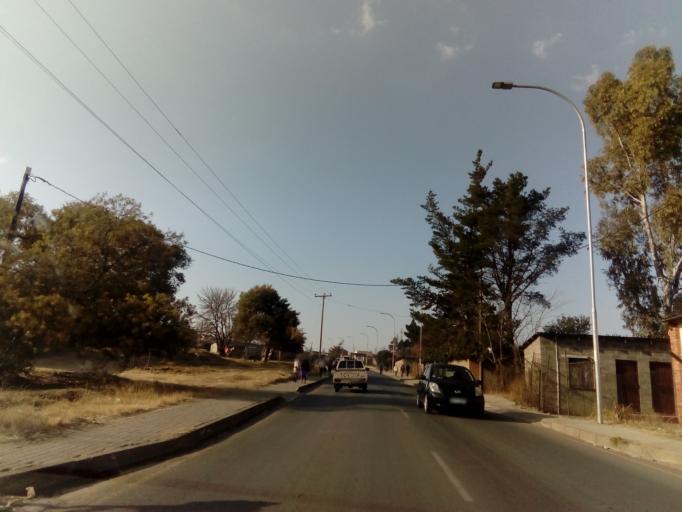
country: LS
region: Maseru
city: Maseru
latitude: -29.3056
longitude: 27.5326
